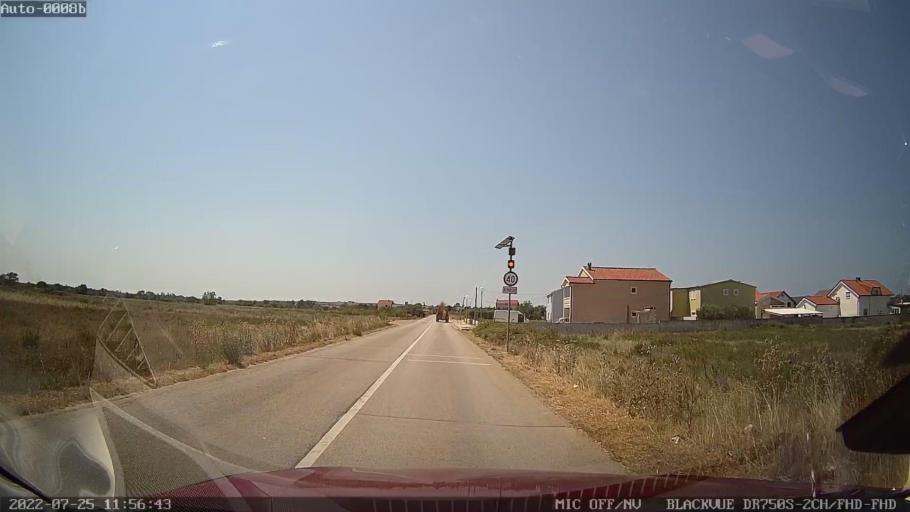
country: HR
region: Zadarska
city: Vrsi
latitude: 44.2476
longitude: 15.2167
